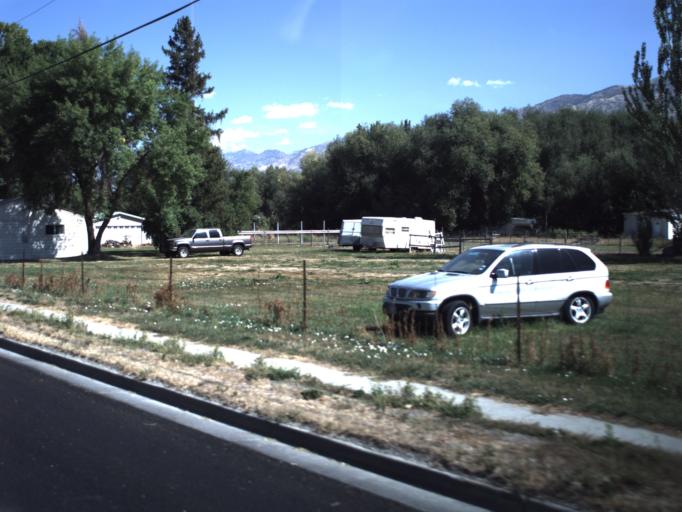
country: US
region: Utah
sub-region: Cache County
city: Nibley
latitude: 41.6806
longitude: -111.8335
